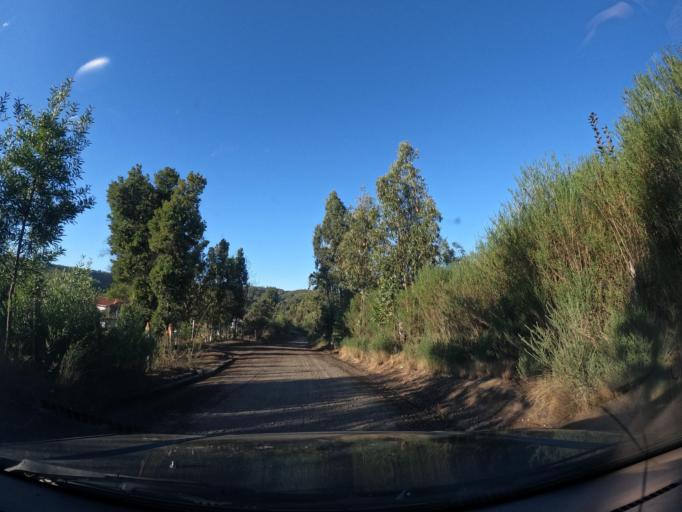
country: CL
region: Biobio
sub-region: Provincia de Concepcion
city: Chiguayante
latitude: -37.0304
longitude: -72.8775
